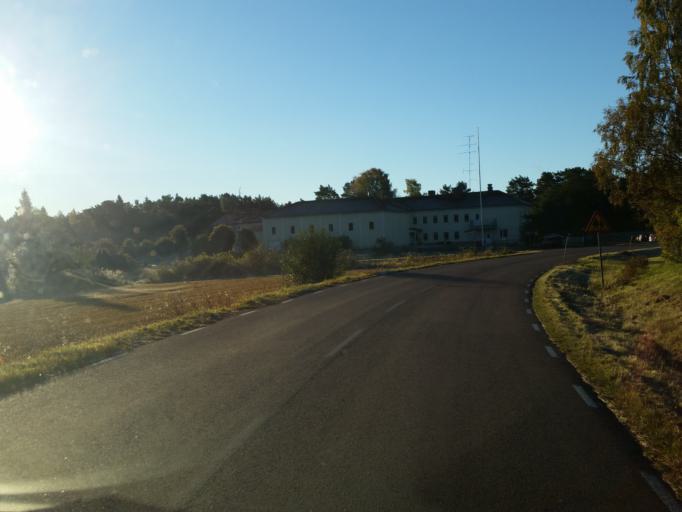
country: AX
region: Alands skaergard
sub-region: Vardoe
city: Vardoe
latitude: 60.2454
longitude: 20.3753
